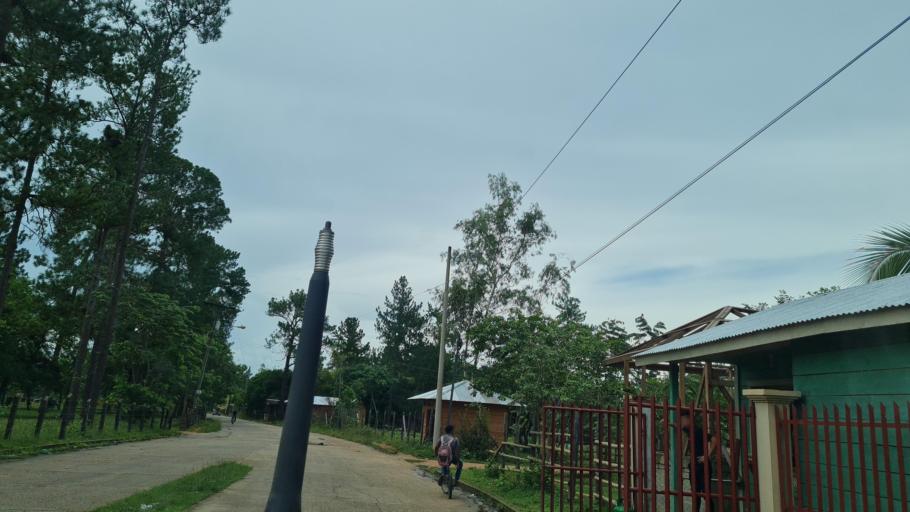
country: NI
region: Atlantico Norte (RAAN)
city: Waspam
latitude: 14.7285
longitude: -83.9698
